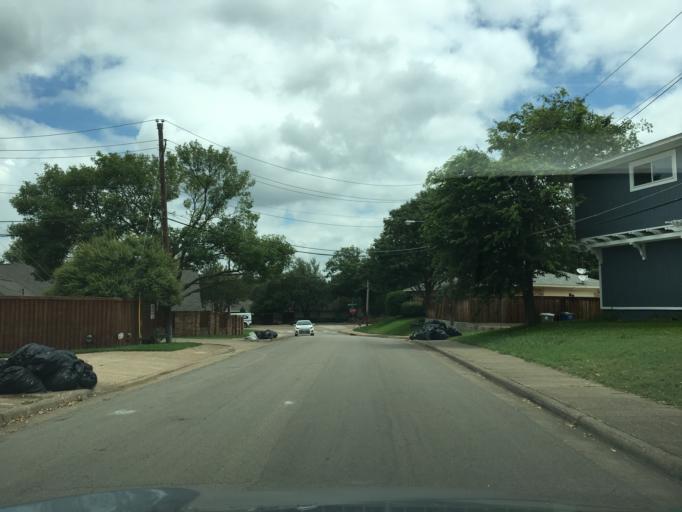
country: US
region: Texas
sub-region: Dallas County
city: Richardson
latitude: 32.8997
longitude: -96.7436
